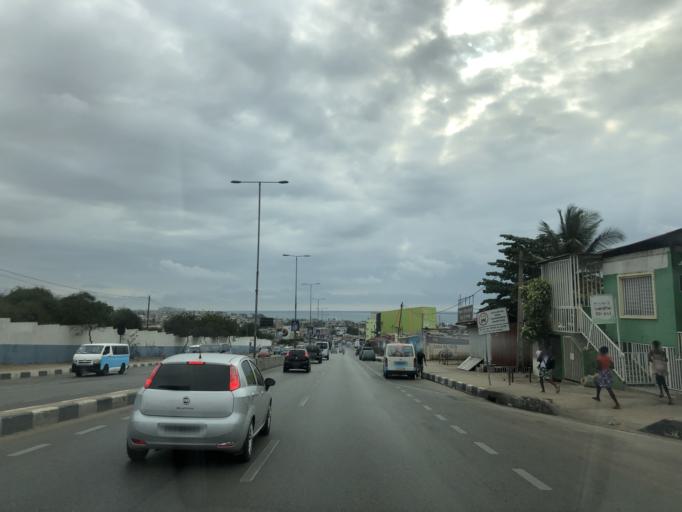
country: AO
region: Luanda
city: Luanda
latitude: -8.8496
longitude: 13.2244
